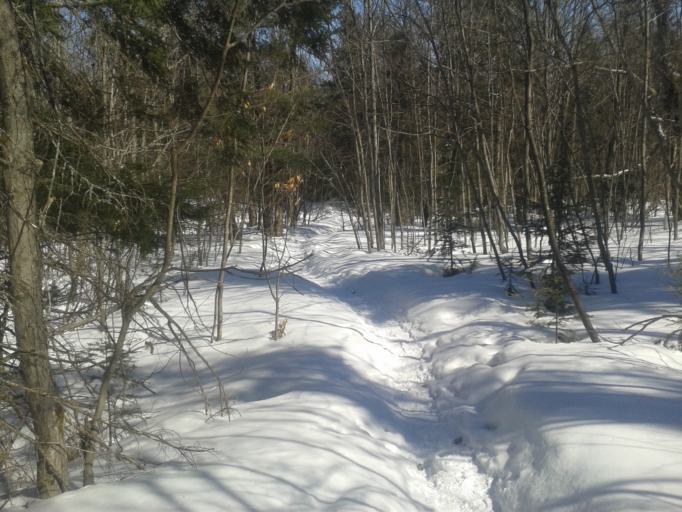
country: CA
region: Ontario
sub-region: Nipissing District
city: North Bay
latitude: 46.3430
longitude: -79.4973
